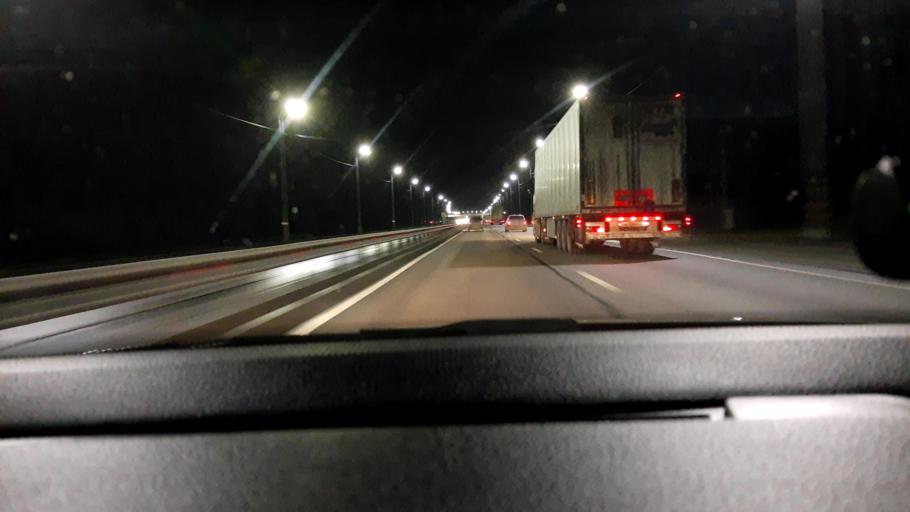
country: RU
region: Vladimir
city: Pokrov
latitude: 55.9060
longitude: 39.0992
